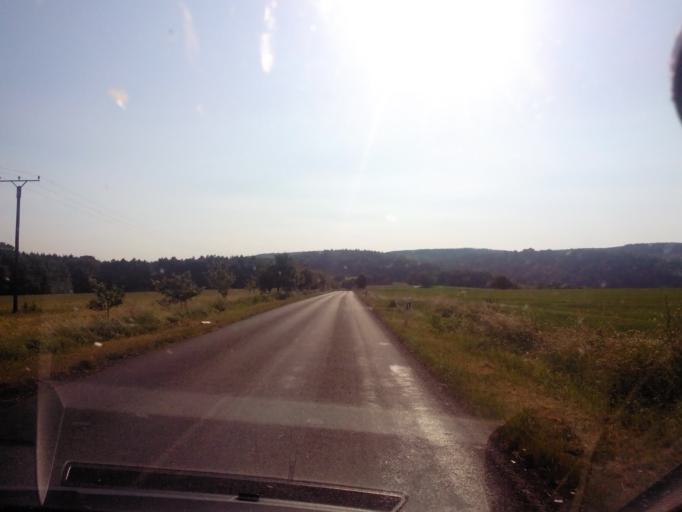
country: DE
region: Saarland
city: Beckingen
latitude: 49.4086
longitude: 6.7396
